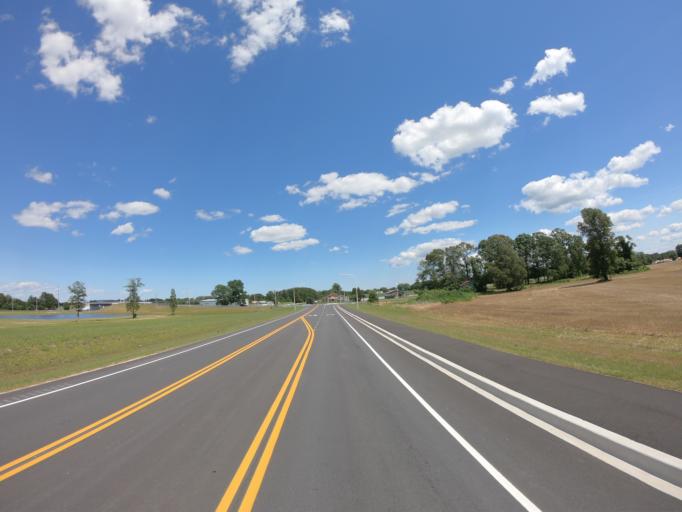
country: US
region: Delaware
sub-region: Sussex County
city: Milford
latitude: 38.9252
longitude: -75.4165
